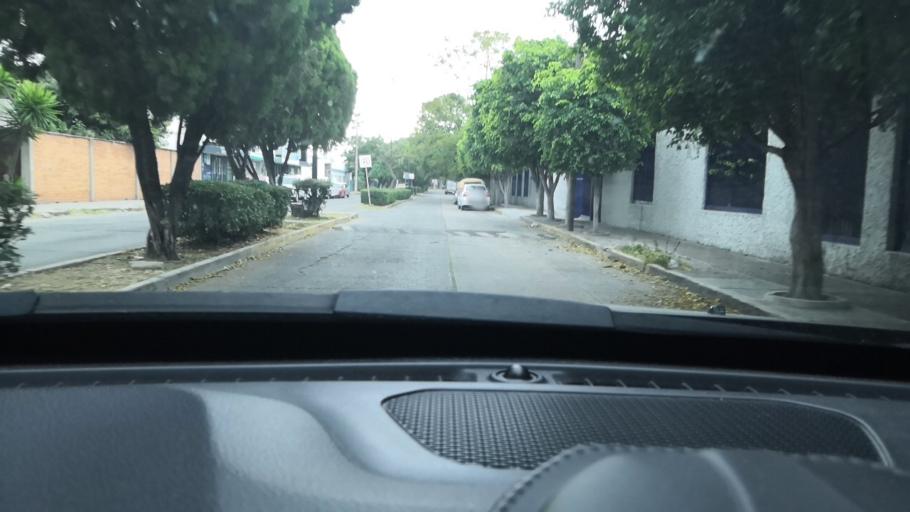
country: MX
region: Guanajuato
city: Leon
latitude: 21.1118
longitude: -101.6695
